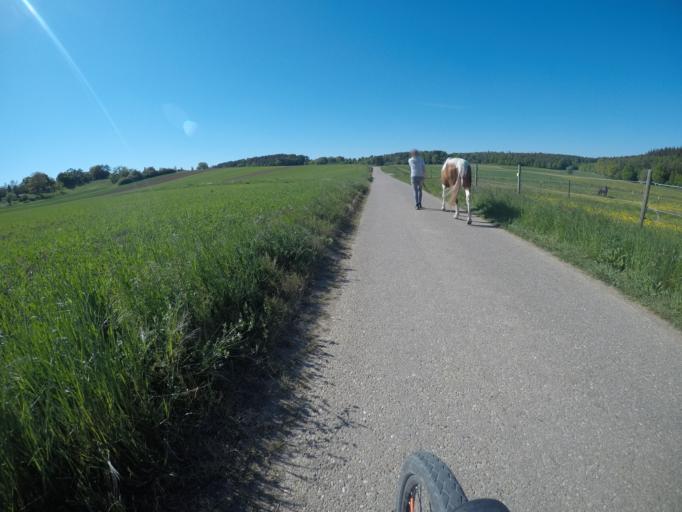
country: DE
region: Baden-Wuerttemberg
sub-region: Karlsruhe Region
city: Heimsheim
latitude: 48.8190
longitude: 8.8557
